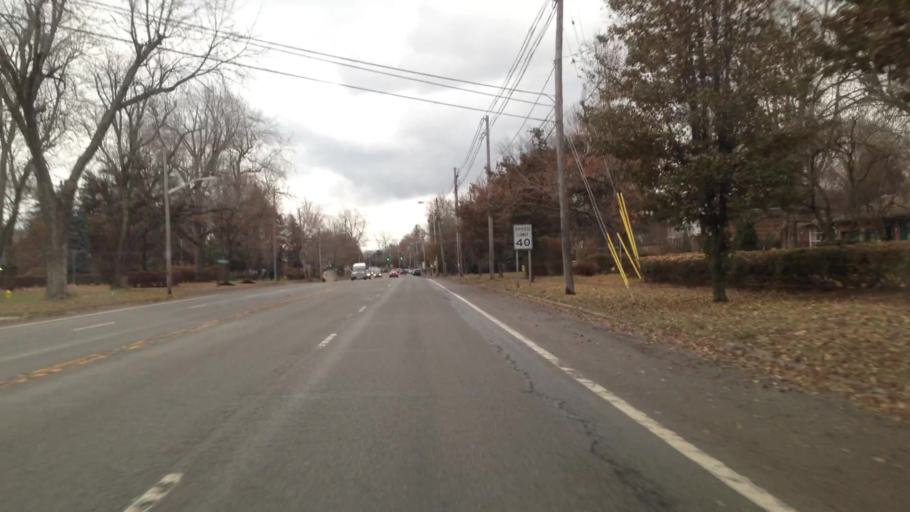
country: US
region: New York
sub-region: Erie County
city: Eggertsville
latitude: 42.9615
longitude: -78.7780
